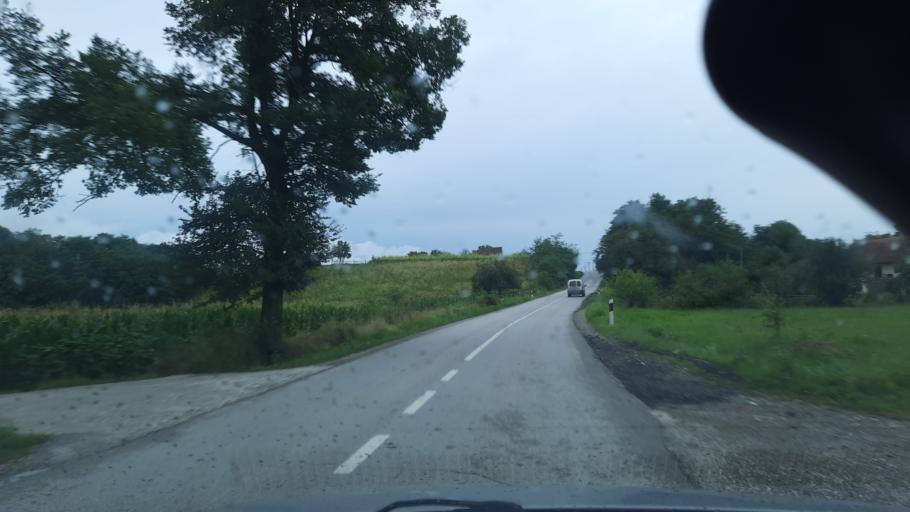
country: RS
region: Central Serbia
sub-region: Raski Okrug
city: Vrnjacka Banja
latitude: 43.7131
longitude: 20.8317
